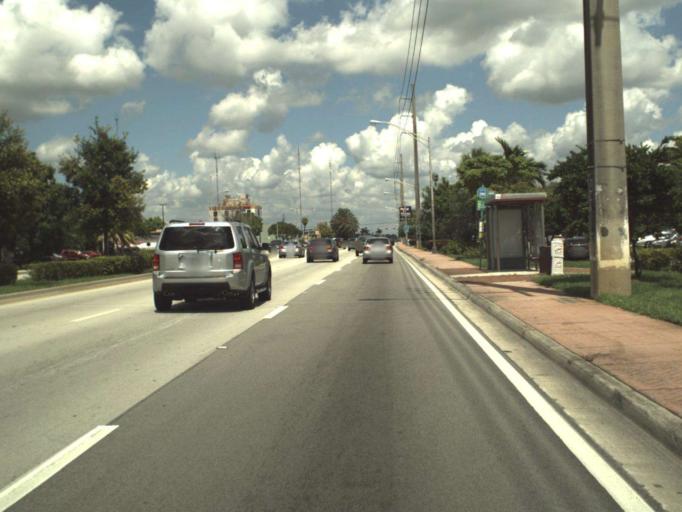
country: US
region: Florida
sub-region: Miami-Dade County
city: Norland
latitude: 25.9391
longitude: -80.2049
